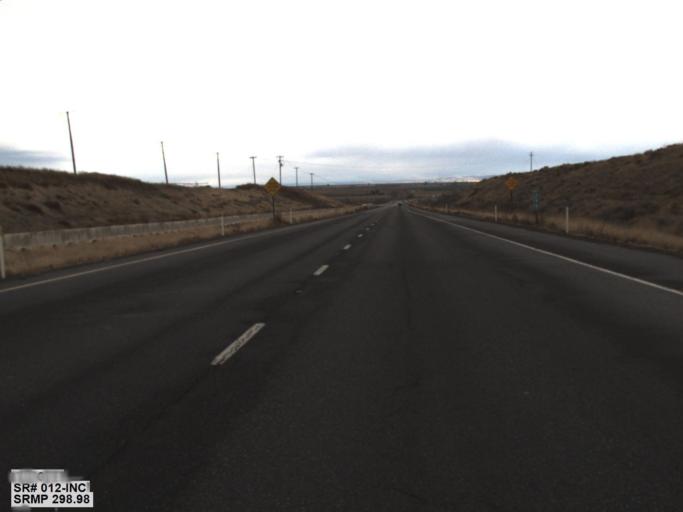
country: US
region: Washington
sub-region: Walla Walla County
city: Burbank
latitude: 46.1717
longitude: -118.9591
